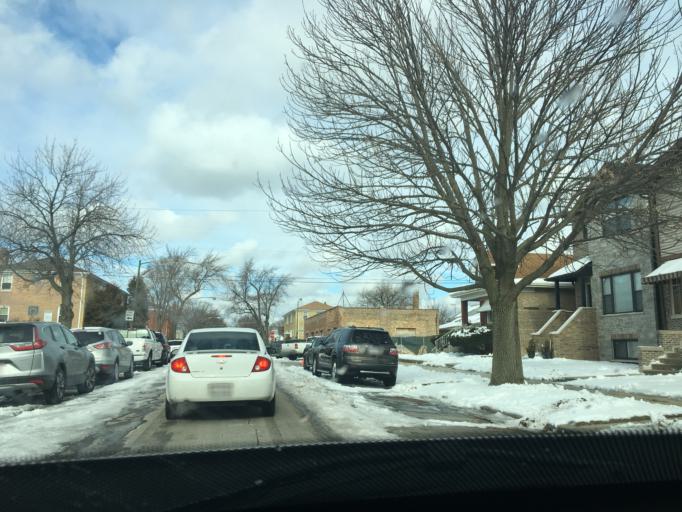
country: US
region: Illinois
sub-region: Cook County
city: Elmwood Park
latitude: 41.9443
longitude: -87.8131
